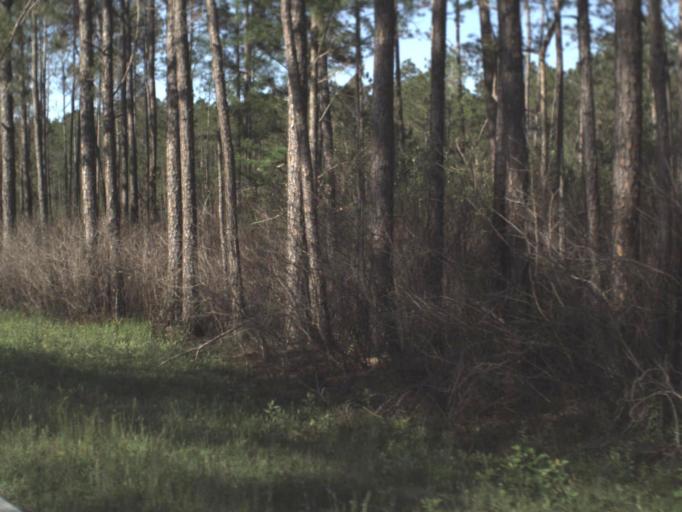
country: US
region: Florida
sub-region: Gulf County
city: Wewahitchka
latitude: 30.0449
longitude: -84.9835
